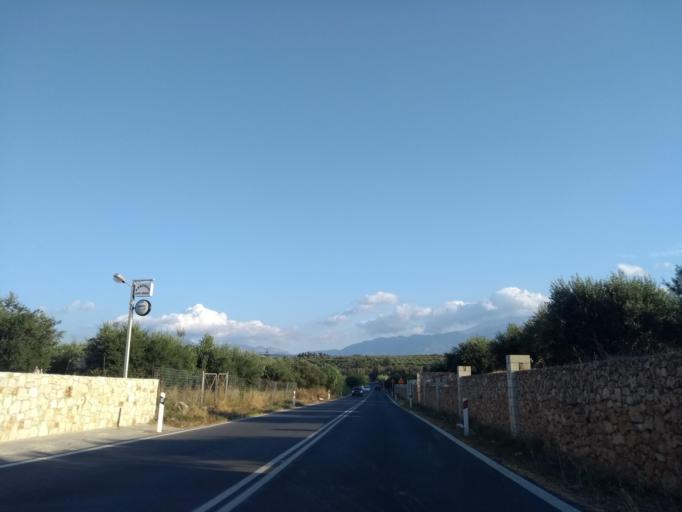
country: GR
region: Crete
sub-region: Nomos Chanias
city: Kalivai
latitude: 35.4635
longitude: 24.1533
